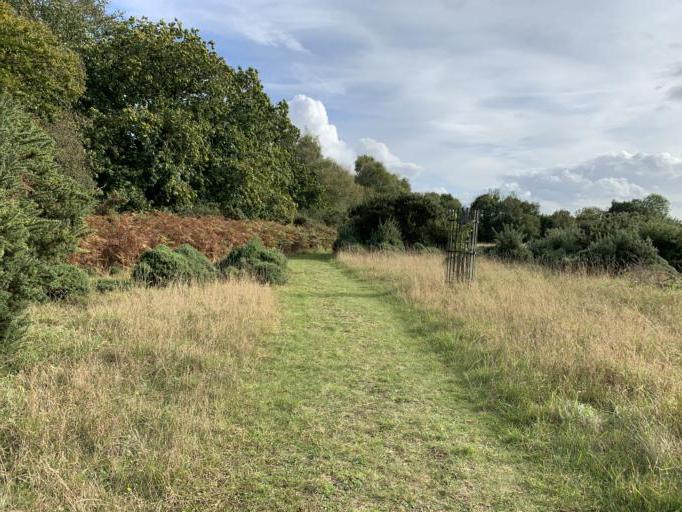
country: GB
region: England
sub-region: Suffolk
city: Aldeburgh
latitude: 52.1263
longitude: 1.5298
